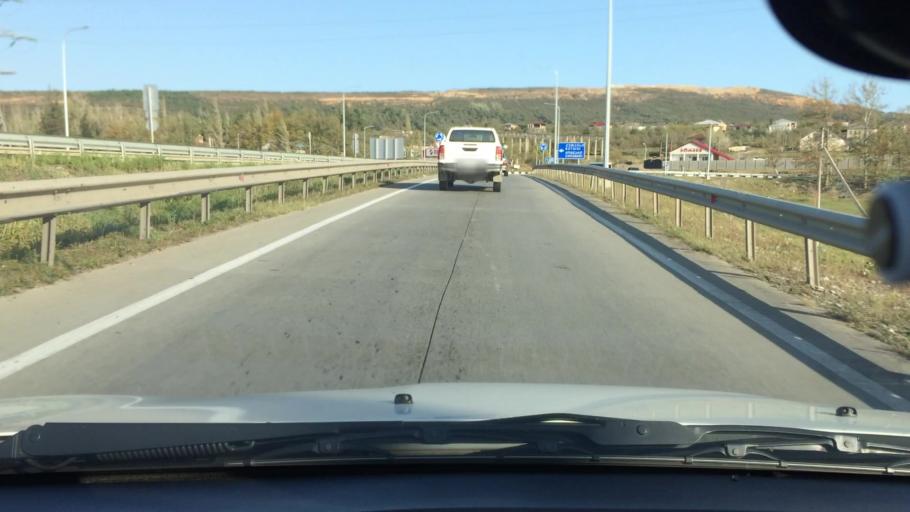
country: GE
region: Imereti
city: Kutaisi
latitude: 42.2121
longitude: 42.8196
